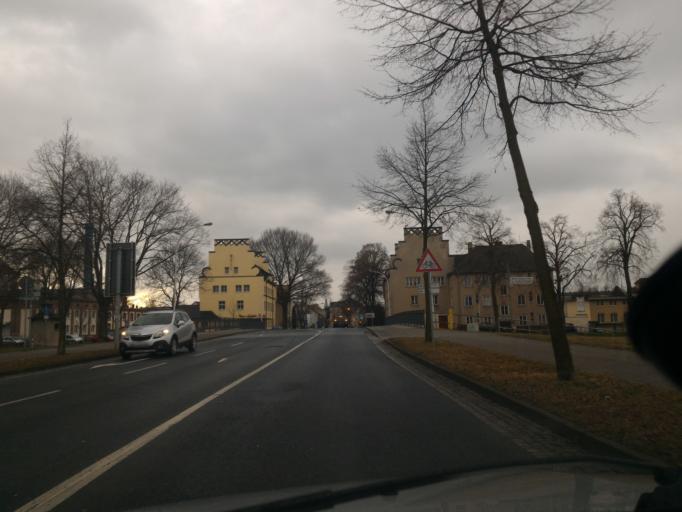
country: DE
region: Saxony
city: Zittau
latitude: 50.8890
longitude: 14.8131
